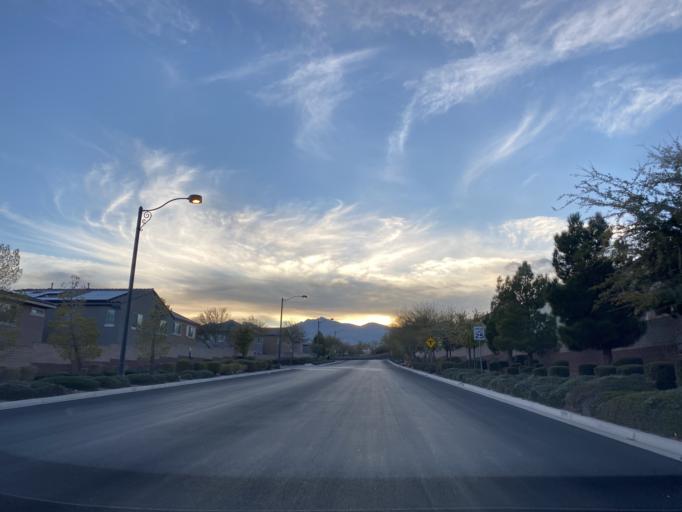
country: US
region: Nevada
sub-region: Clark County
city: Summerlin South
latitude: 36.3036
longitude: -115.3247
